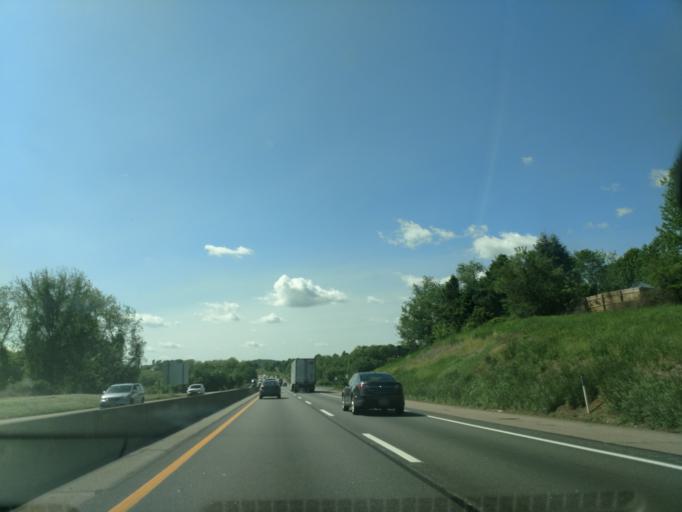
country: US
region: Pennsylvania
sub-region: Chester County
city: Downingtown
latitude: 40.0786
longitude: -75.7024
